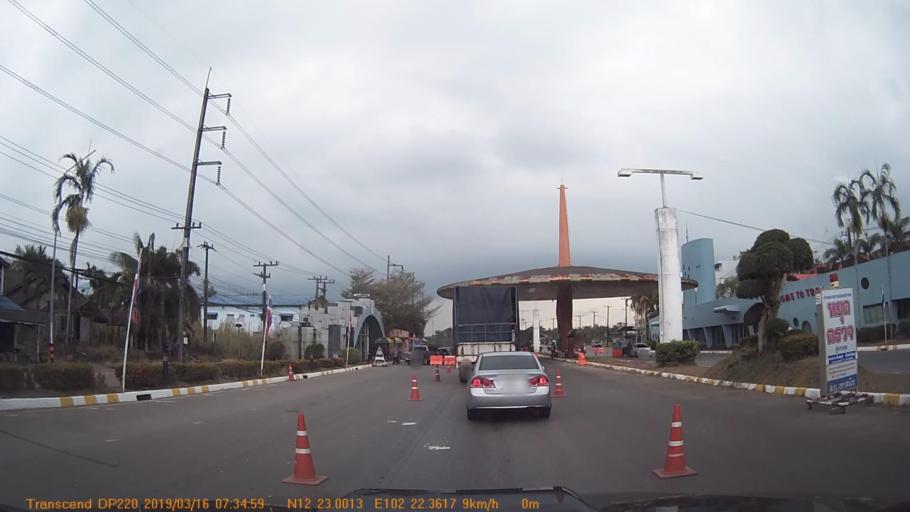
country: TH
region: Trat
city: Khao Saming
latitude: 12.3808
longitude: 102.3748
